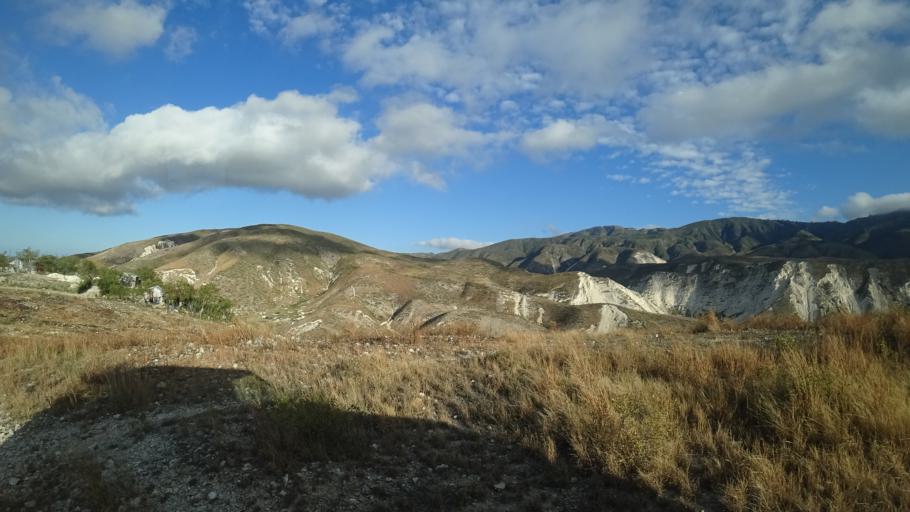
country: HT
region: Ouest
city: Croix des Bouquets
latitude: 18.6729
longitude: -72.2597
